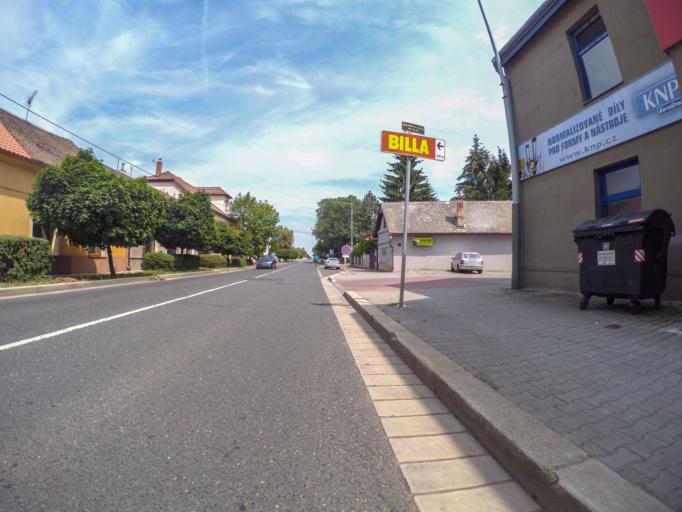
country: CZ
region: Praha
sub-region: Praha 19
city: Kbely
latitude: 50.1305
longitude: 14.5487
